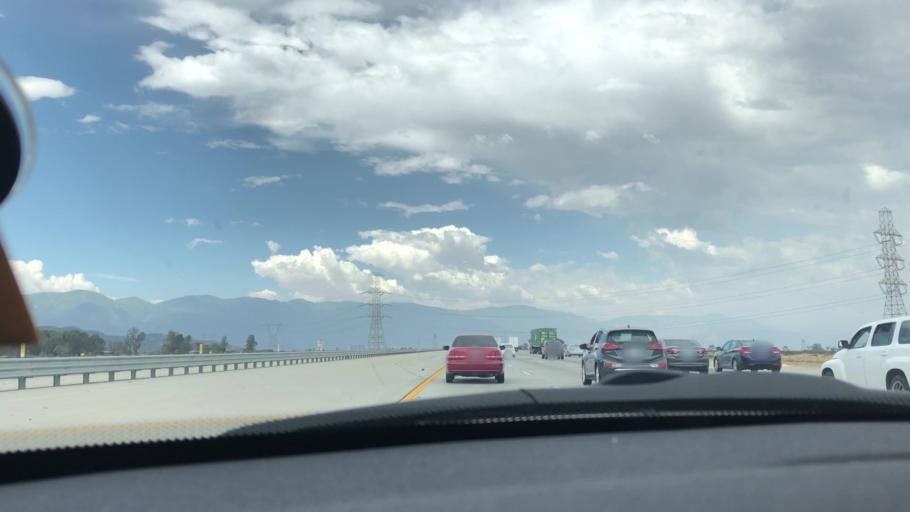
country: US
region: California
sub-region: San Bernardino County
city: Fontana
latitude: 34.1735
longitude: -117.4489
